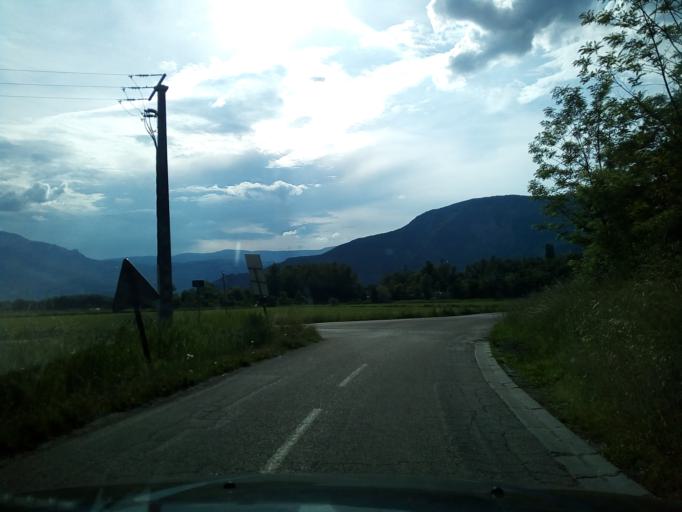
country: FR
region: Rhone-Alpes
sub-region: Departement de l'Isere
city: Meylan
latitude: 45.2049
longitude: 5.7934
